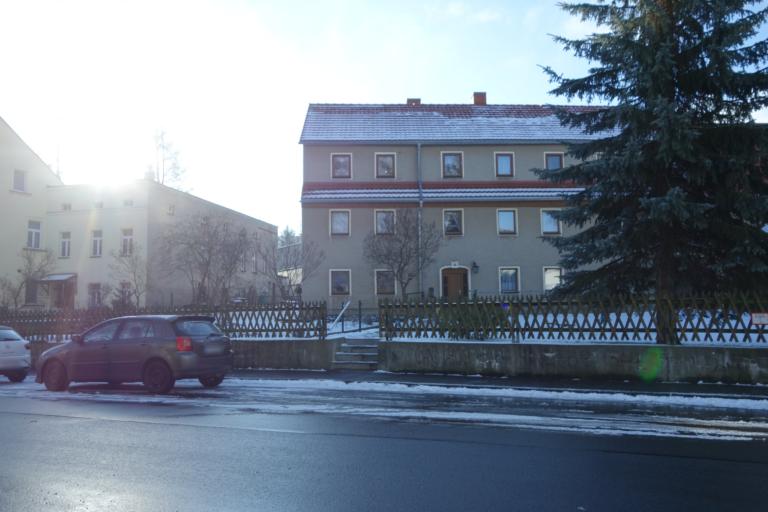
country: DE
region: Saxony
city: Freiberg
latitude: 50.9194
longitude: 13.3314
